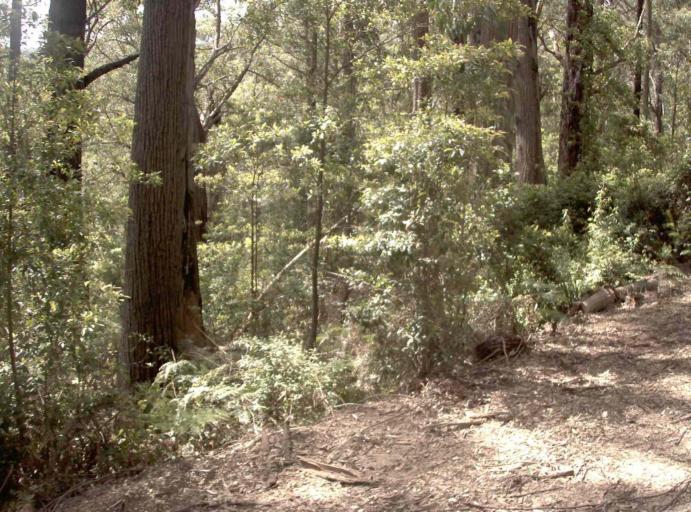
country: AU
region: Victoria
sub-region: East Gippsland
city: Lakes Entrance
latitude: -37.5871
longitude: 148.7257
